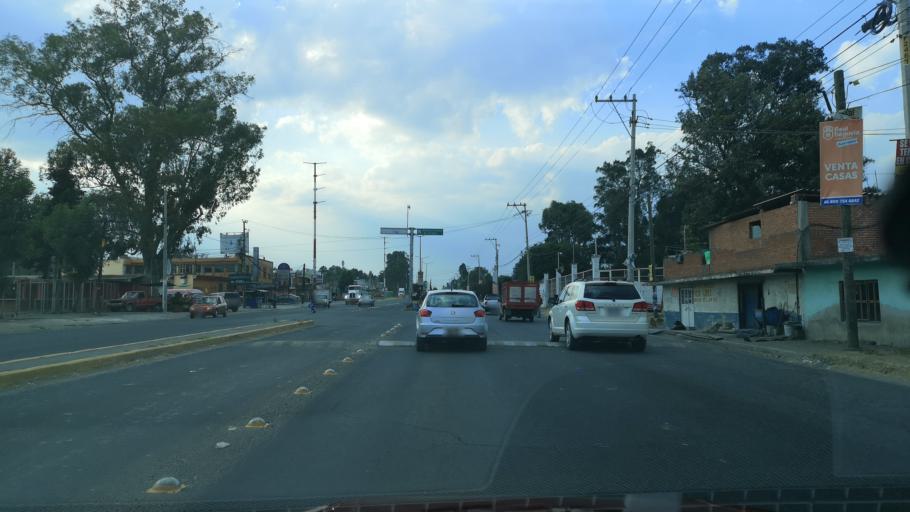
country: MX
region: Puebla
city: Cuanala
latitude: 19.1016
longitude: -98.3462
